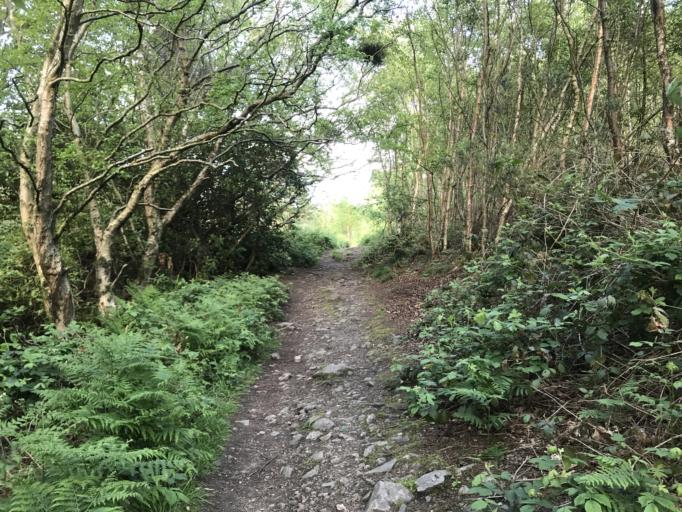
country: IE
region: Leinster
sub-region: Fingal County
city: Howth
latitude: 53.3767
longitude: -6.0783
